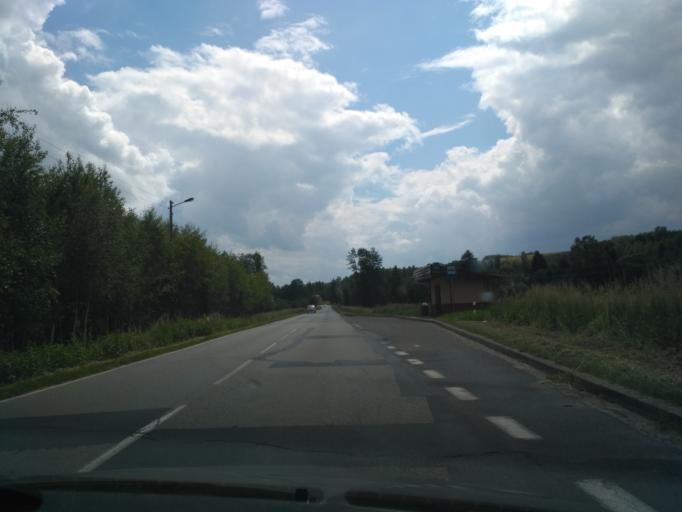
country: PL
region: Subcarpathian Voivodeship
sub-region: Powiat rzeszowski
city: Blazowa
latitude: 49.9293
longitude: 22.1208
